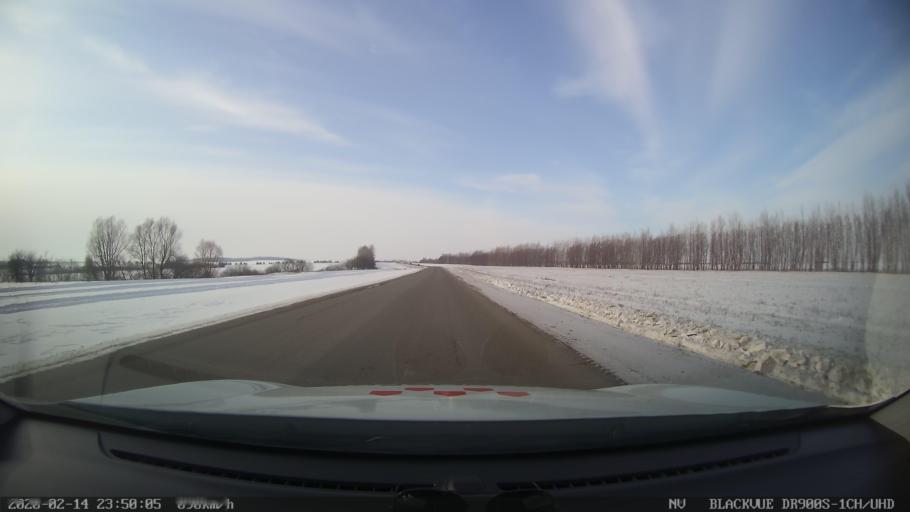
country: RU
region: Tatarstan
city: Kuybyshevskiy Zaton
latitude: 55.2573
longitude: 49.1679
